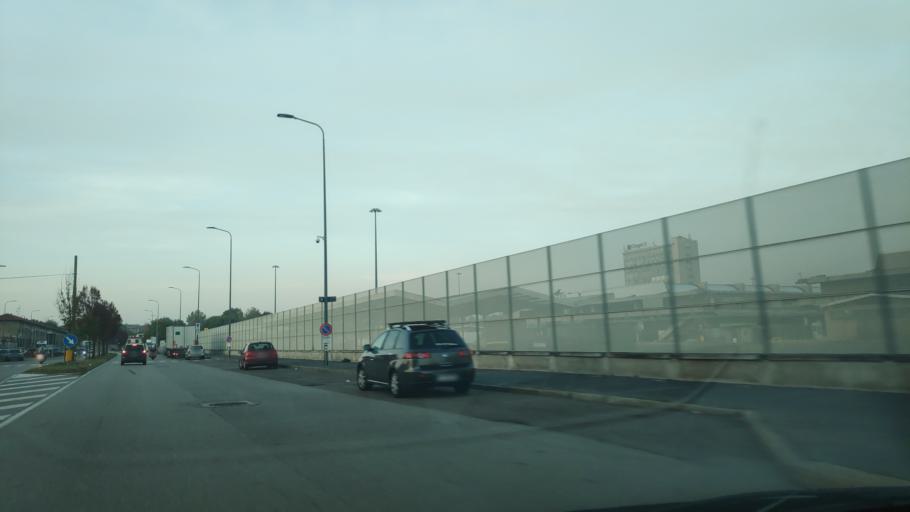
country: IT
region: Lombardy
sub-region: Citta metropolitana di Milano
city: Chiaravalle
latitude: 45.4529
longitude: 9.2293
